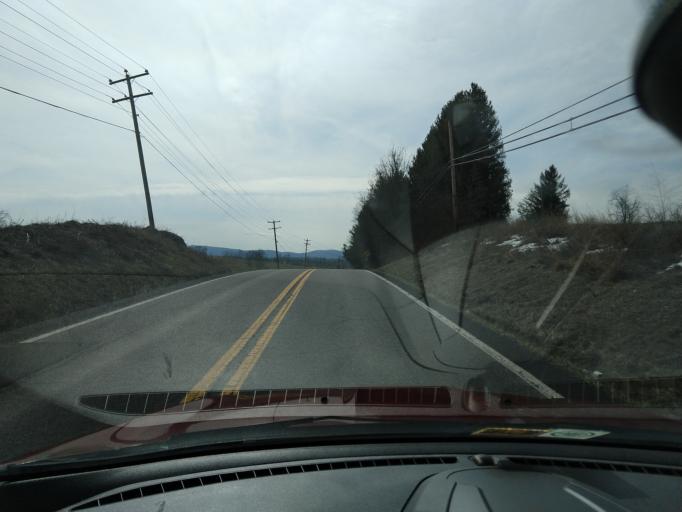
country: US
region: West Virginia
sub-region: Greenbrier County
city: Lewisburg
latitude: 37.8826
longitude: -80.4132
